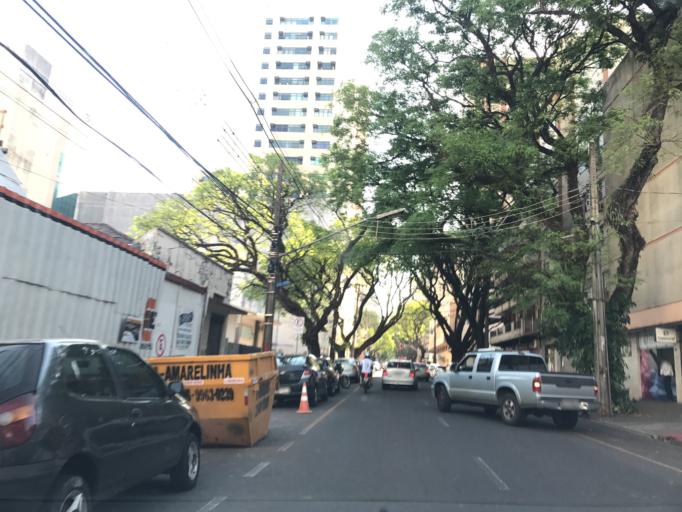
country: BR
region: Parana
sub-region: Maringa
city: Maringa
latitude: -23.4219
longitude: -51.9314
